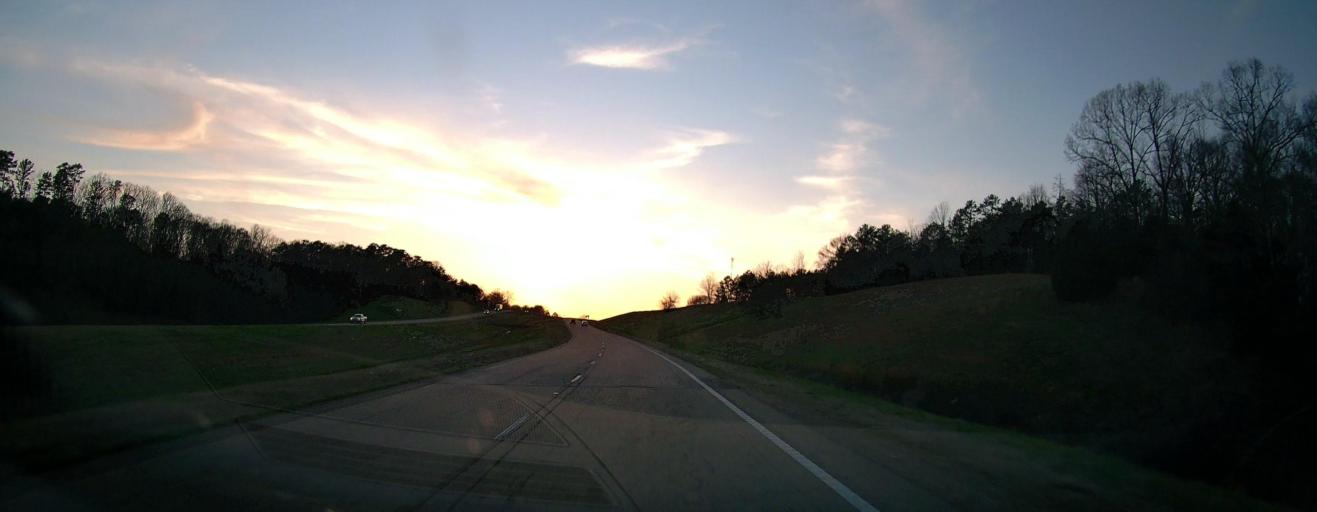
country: US
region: Mississippi
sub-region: Tippah County
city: Ripley
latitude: 34.9463
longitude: -88.7929
